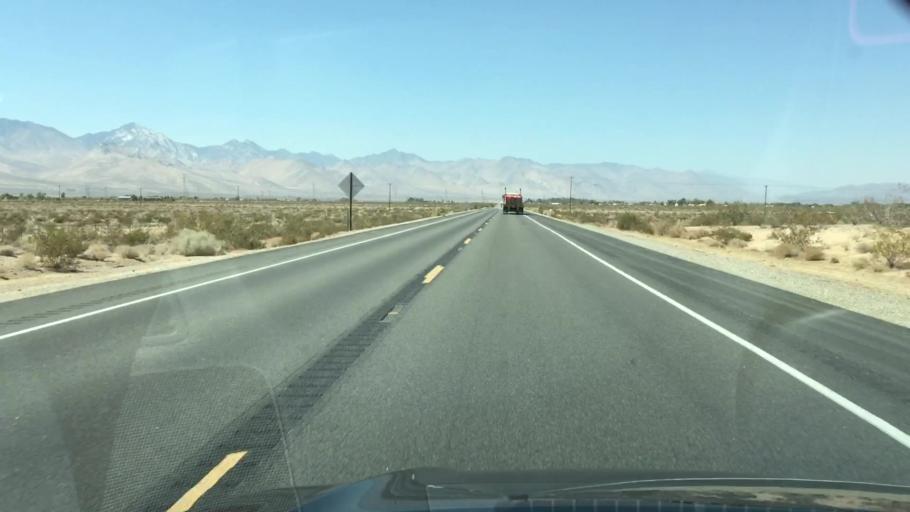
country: US
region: California
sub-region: Kern County
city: China Lake Acres
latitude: 35.6201
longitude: -117.7734
